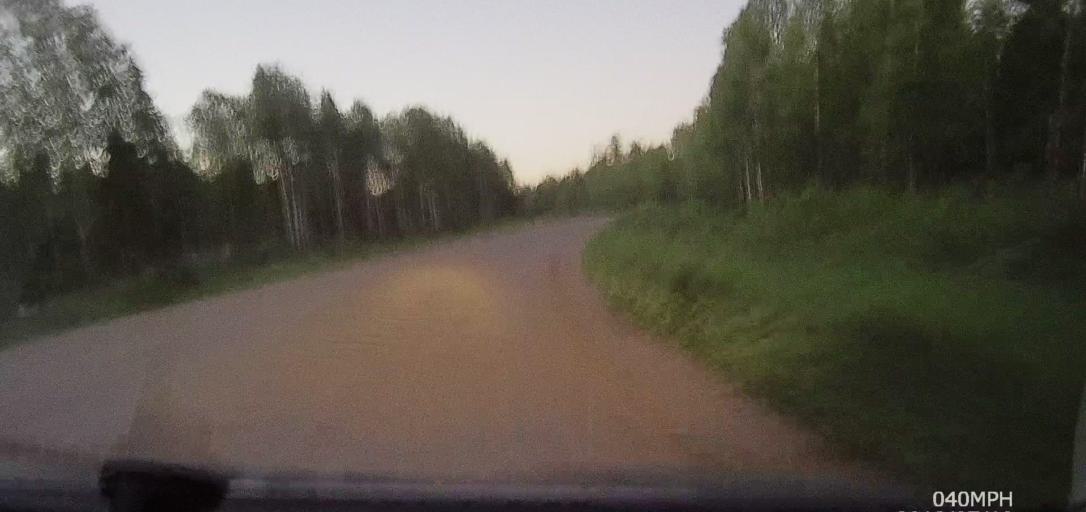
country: RU
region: Arkhangelskaya
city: Pinega
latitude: 64.4340
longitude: 43.1366
